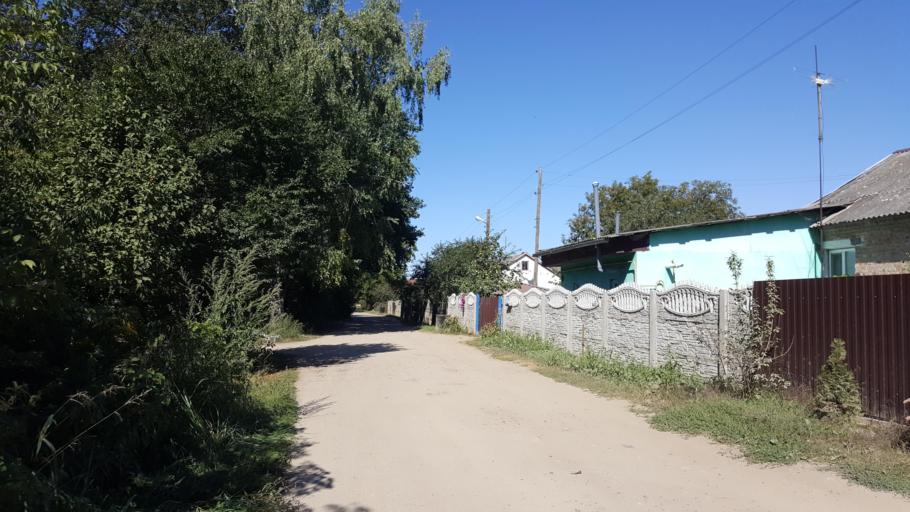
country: BY
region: Brest
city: Vysokaye
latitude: 52.2588
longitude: 23.4944
